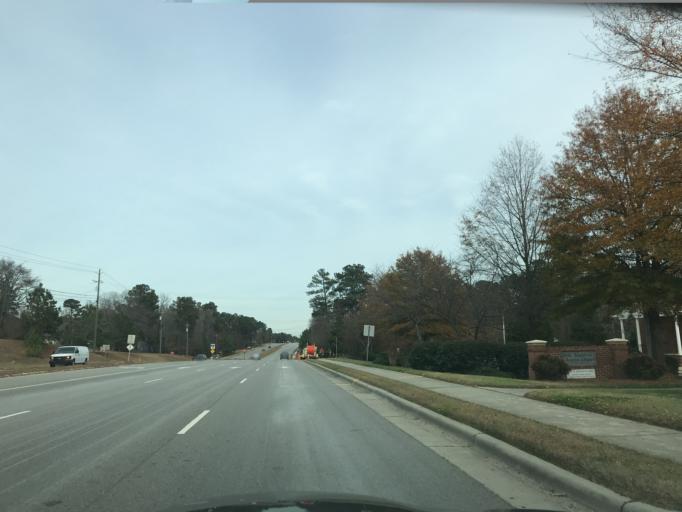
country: US
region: North Carolina
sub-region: Wake County
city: Knightdale
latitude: 35.8499
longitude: -78.5615
